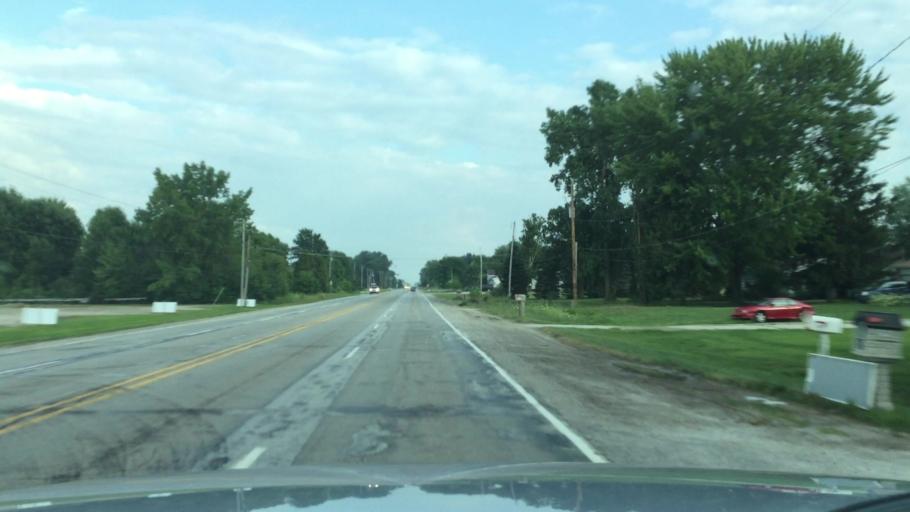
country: US
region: Michigan
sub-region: Saginaw County
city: Birch Run
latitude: 43.2664
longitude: -83.7816
